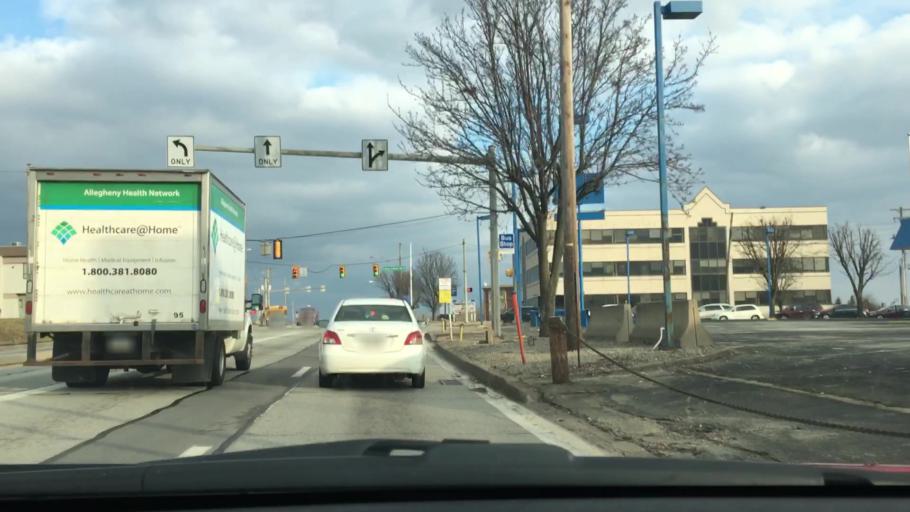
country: US
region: Pennsylvania
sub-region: Allegheny County
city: Pleasant Hills
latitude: 40.3502
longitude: -79.9279
